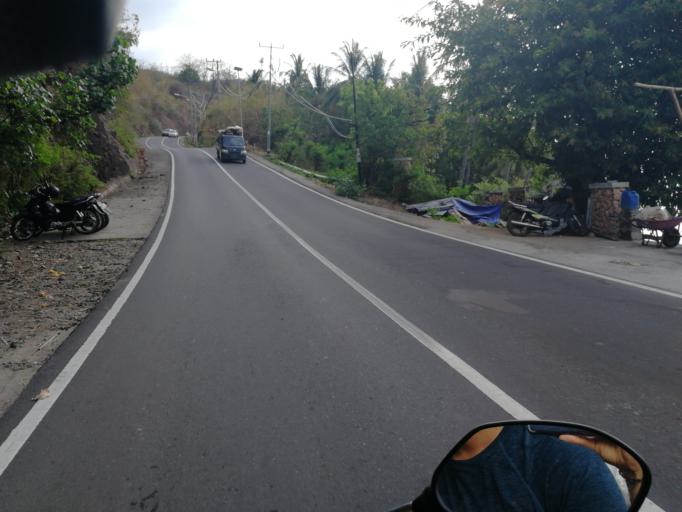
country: ID
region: West Nusa Tenggara
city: Karangsubagan
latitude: -8.4357
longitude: 116.0422
